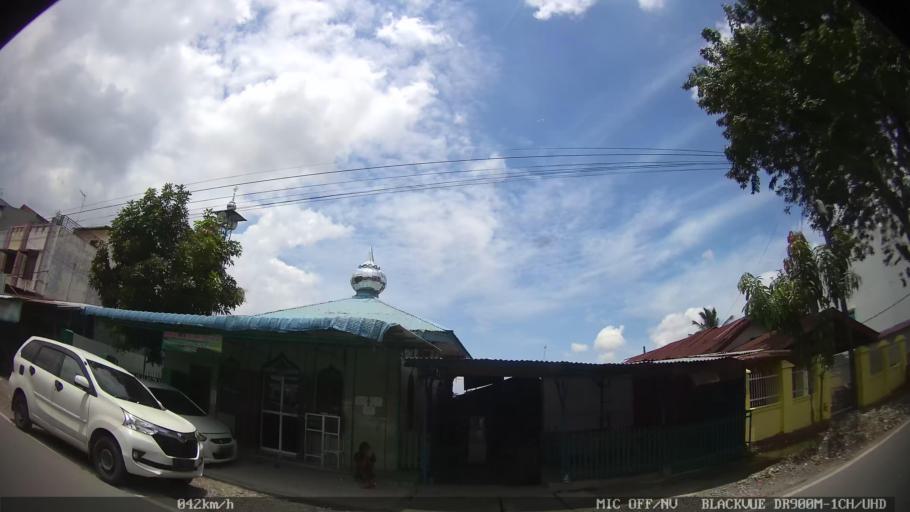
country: ID
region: North Sumatra
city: Medan
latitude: 3.6163
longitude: 98.6941
